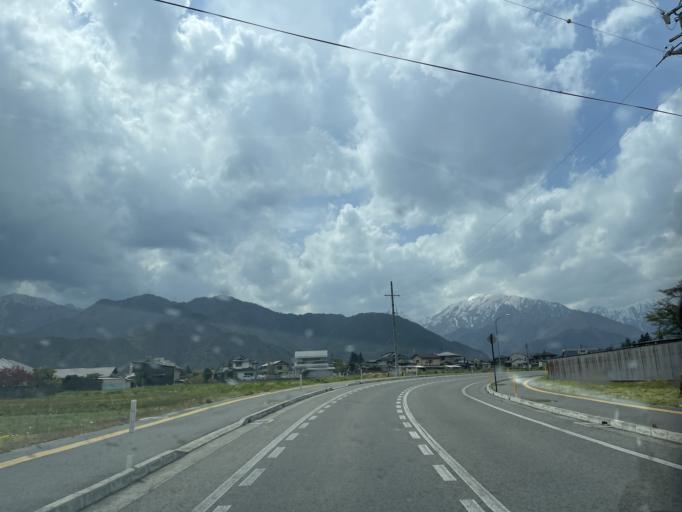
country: JP
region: Nagano
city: Omachi
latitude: 36.4993
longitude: 137.8514
